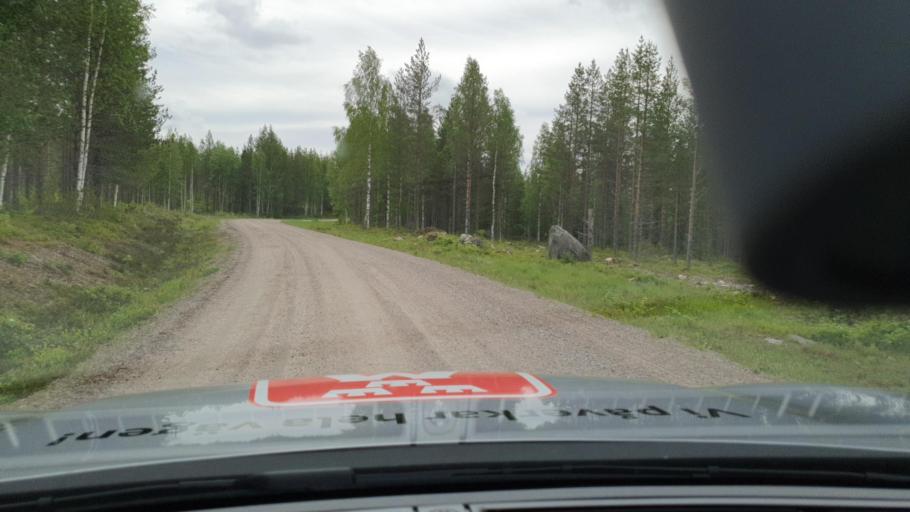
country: SE
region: Norrbotten
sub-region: Kalix Kommun
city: Kalix
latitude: 66.0485
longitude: 23.3594
